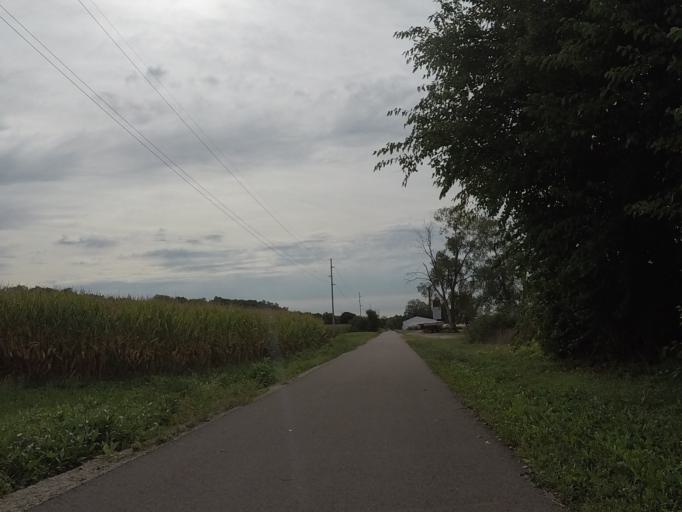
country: US
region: Wisconsin
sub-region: Sauk County
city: Prairie du Sac
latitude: 43.3188
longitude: -89.7397
